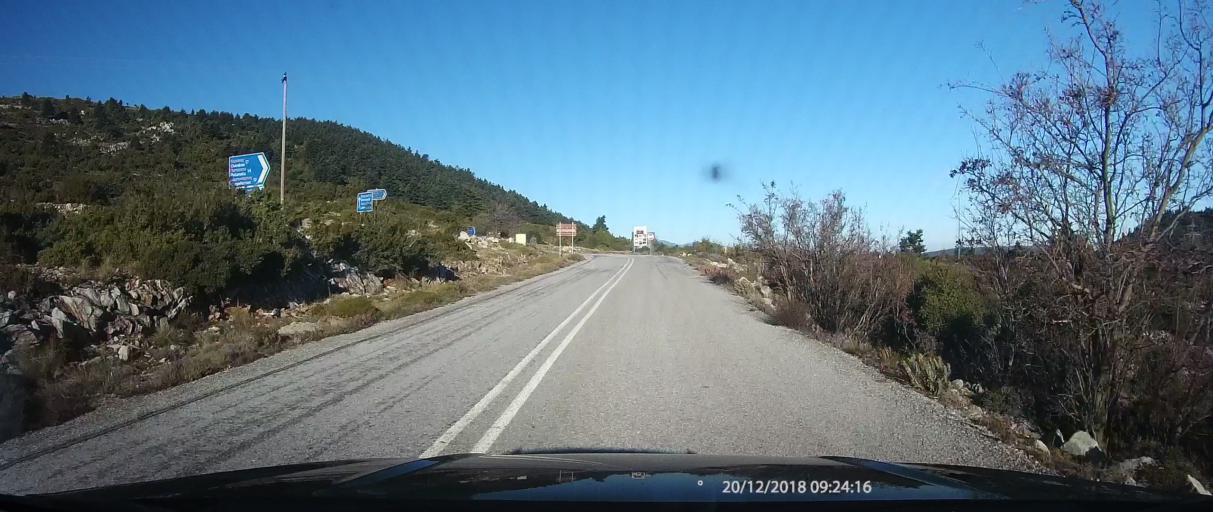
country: GR
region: Peloponnese
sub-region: Nomos Lakonias
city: Molaoi
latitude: 36.9638
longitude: 22.8913
